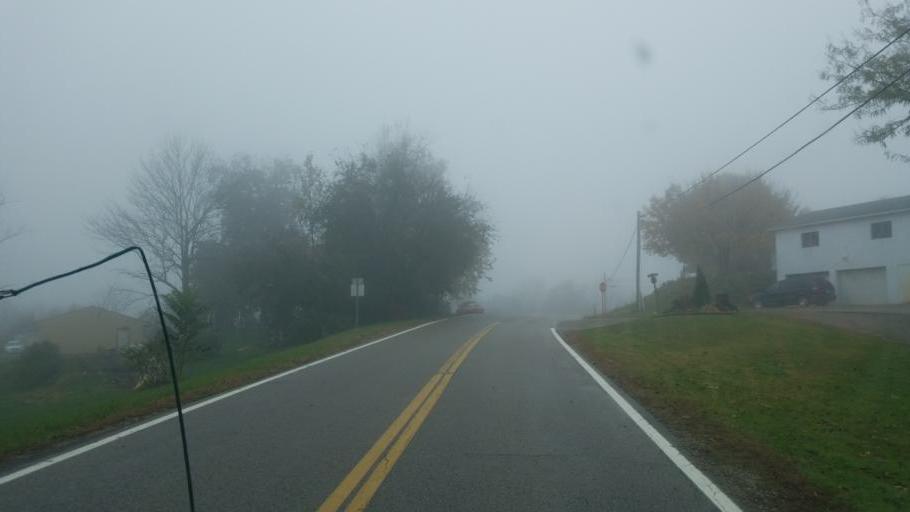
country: US
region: Ohio
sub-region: Morgan County
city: McConnelsville
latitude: 39.6232
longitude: -81.8812
